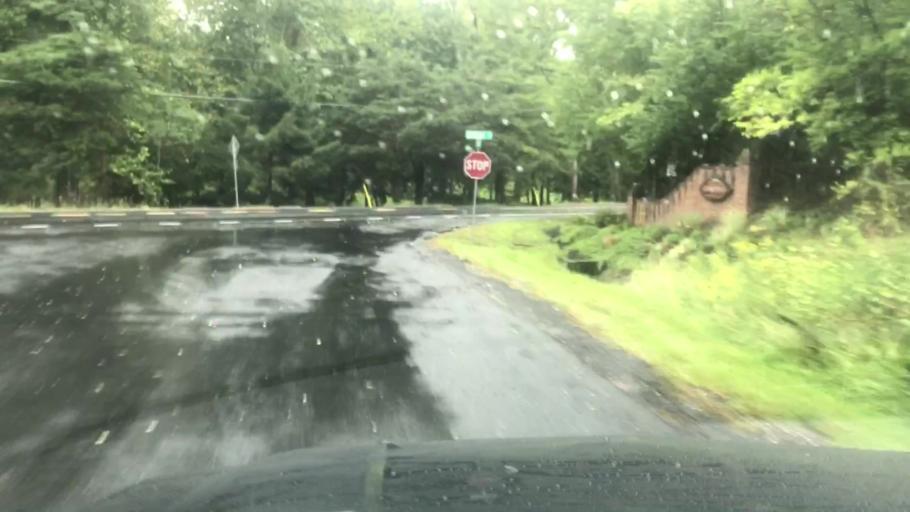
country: US
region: Pennsylvania
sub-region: Cumberland County
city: Shiremanstown
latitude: 40.1777
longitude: -76.9447
